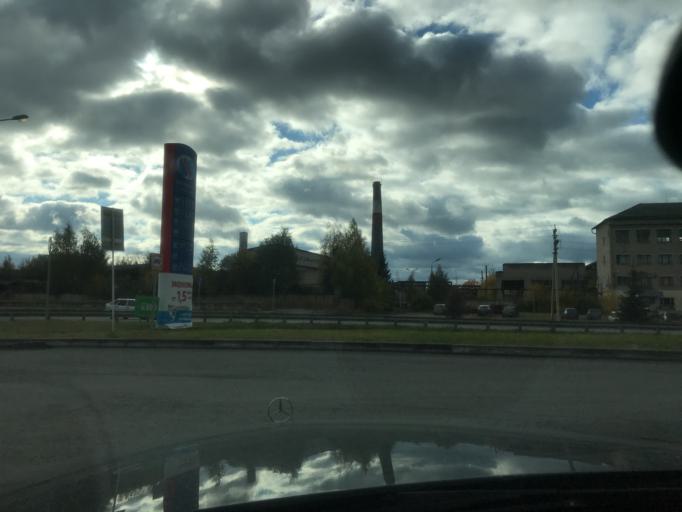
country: RU
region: Pskov
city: Opochka
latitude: 56.7108
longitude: 28.6913
